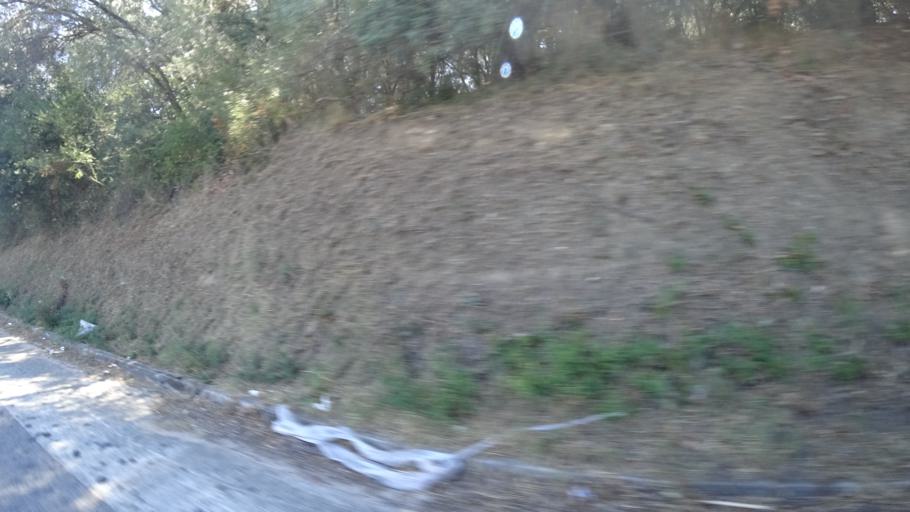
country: FR
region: Corsica
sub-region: Departement de la Corse-du-Sud
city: Ajaccio
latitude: 41.9409
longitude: 8.7364
